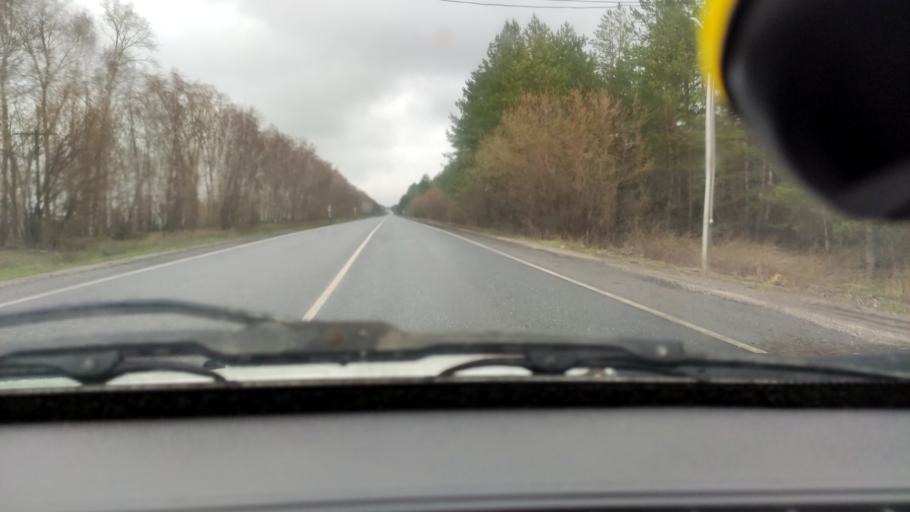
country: RU
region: Samara
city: Povolzhskiy
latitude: 53.6094
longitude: 49.6146
